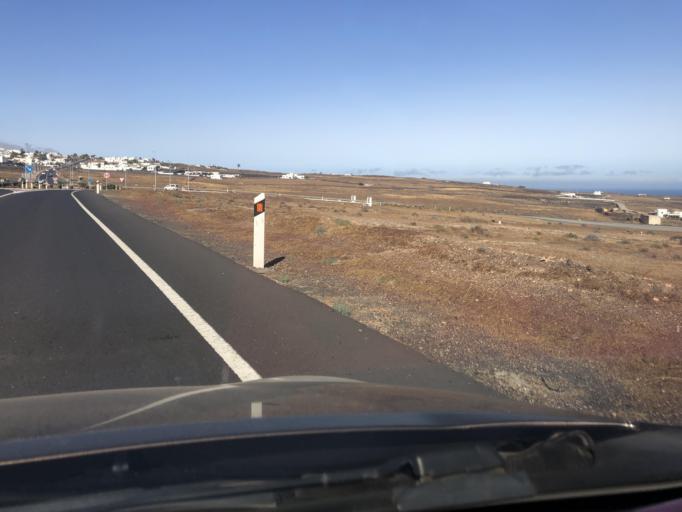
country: ES
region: Canary Islands
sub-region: Provincia de Las Palmas
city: Puerto del Carmen
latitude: 28.9420
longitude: -13.7071
